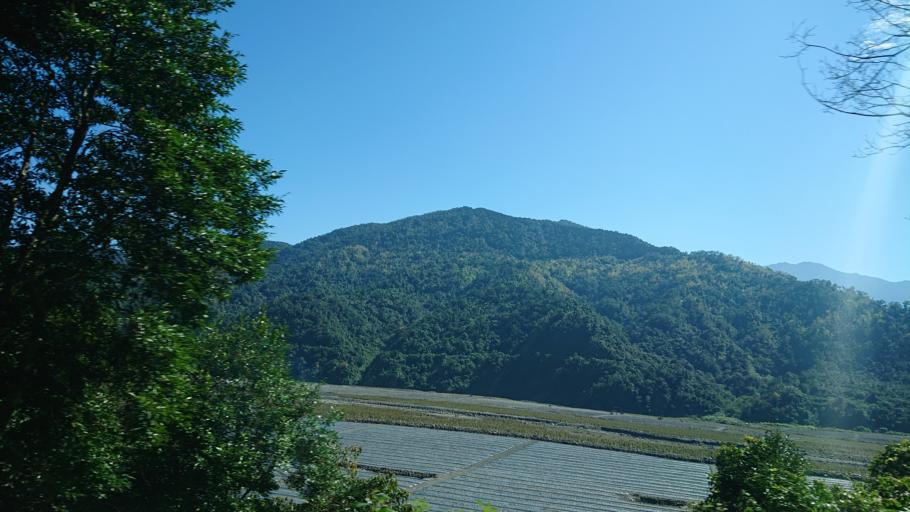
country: TW
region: Taiwan
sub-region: Yilan
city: Yilan
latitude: 24.5852
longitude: 121.4996
